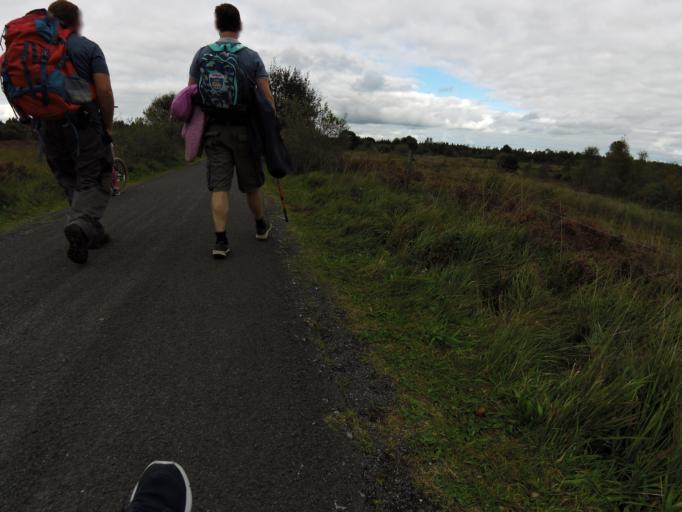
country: IE
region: Leinster
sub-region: Uibh Fhaili
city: Ferbane
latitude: 53.2211
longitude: -7.7320
